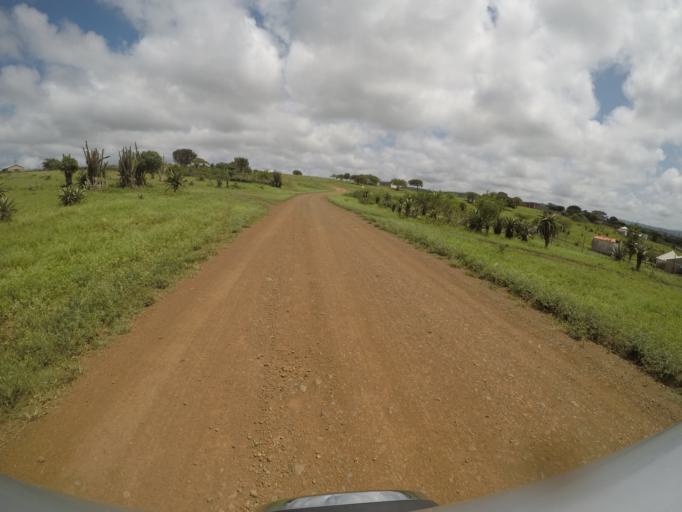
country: ZA
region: KwaZulu-Natal
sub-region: uThungulu District Municipality
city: Empangeni
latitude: -28.5764
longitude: 31.8358
